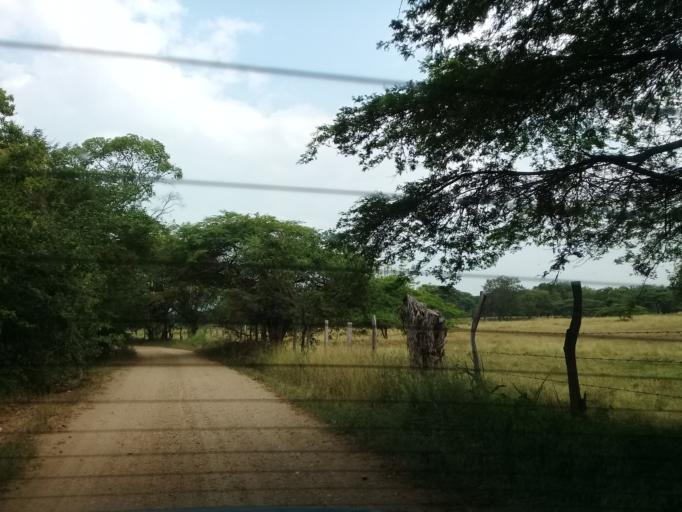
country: CO
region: Cundinamarca
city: Agua de Dios
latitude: 4.3638
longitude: -74.7223
